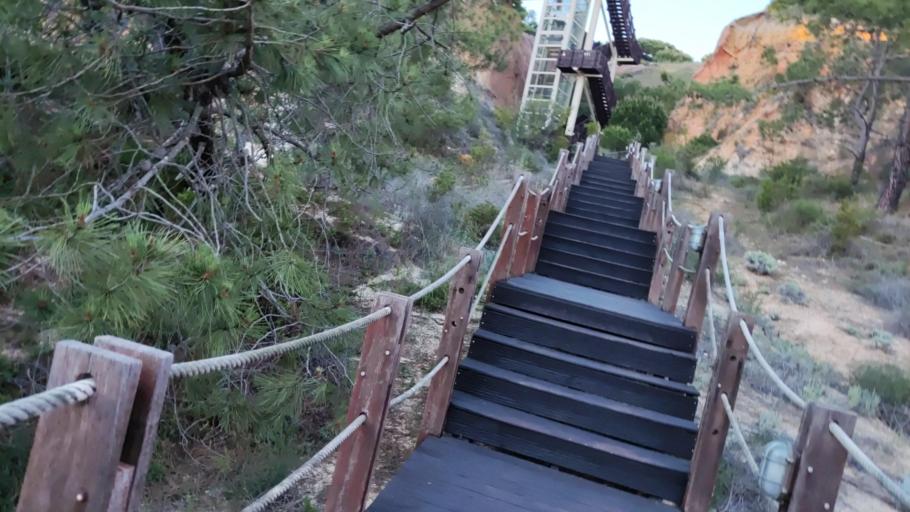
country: PT
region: Faro
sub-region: Loule
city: Boliqueime
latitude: 37.0910
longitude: -8.1787
